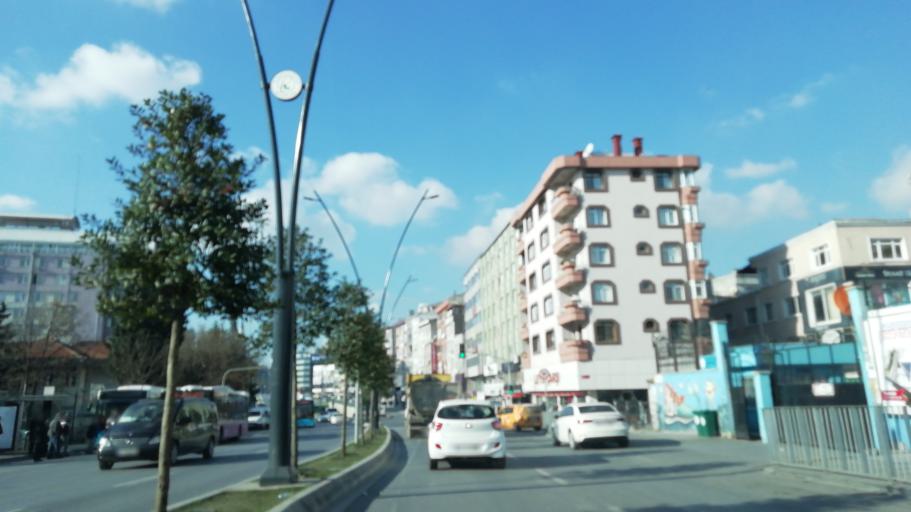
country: TR
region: Istanbul
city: Esenler
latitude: 41.0581
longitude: 28.9169
